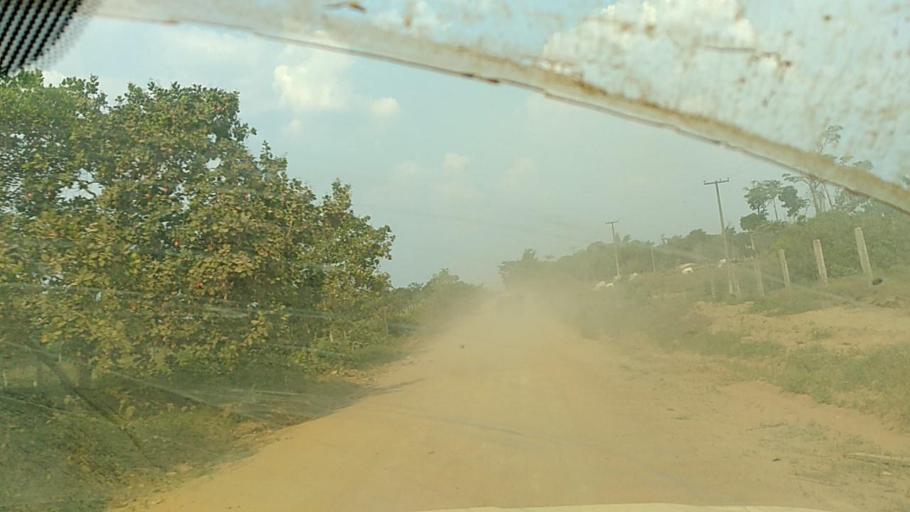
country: BR
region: Rondonia
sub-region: Porto Velho
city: Porto Velho
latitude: -8.6829
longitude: -63.2307
